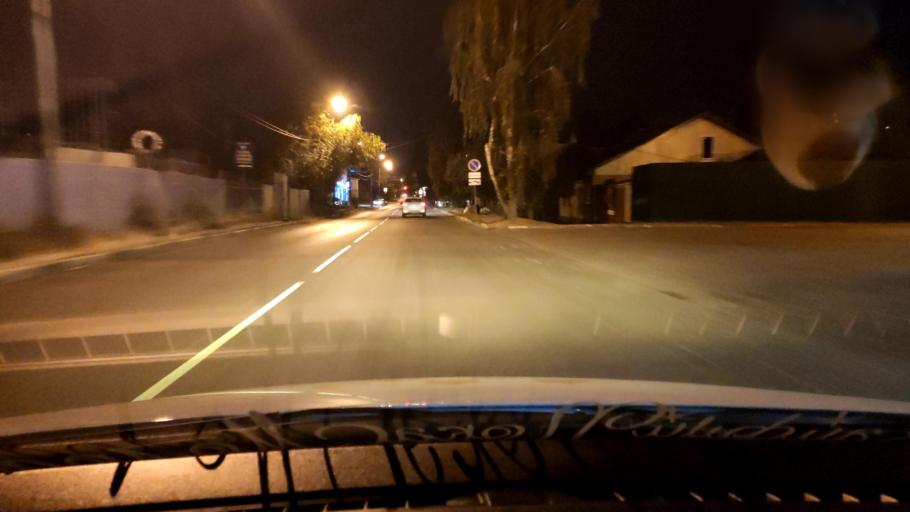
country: RU
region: Voronezj
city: Voronezh
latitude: 51.6671
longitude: 39.1708
